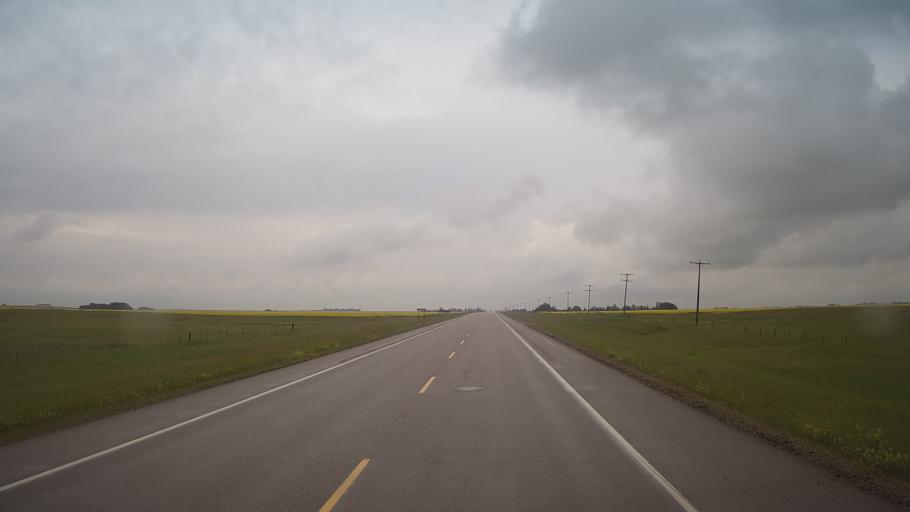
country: CA
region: Saskatchewan
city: Unity
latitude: 52.4349
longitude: -109.0025
